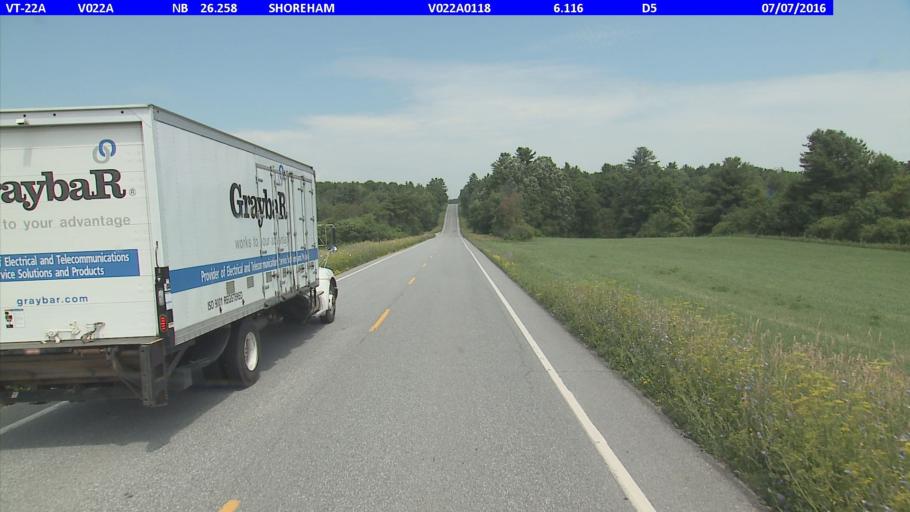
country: US
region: New York
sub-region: Essex County
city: Ticonderoga
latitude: 43.9370
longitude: -73.3104
